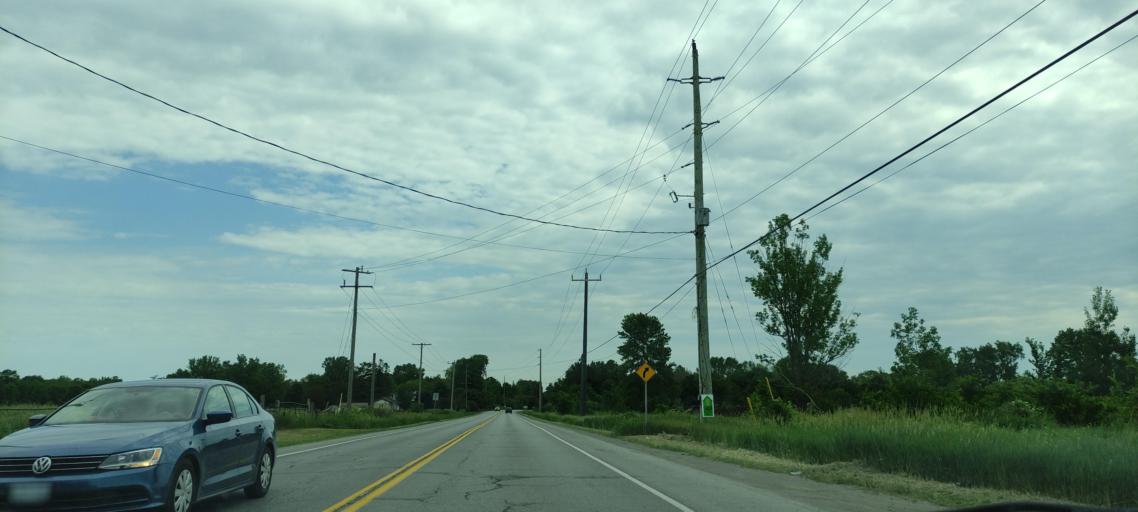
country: CA
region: Ontario
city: Quinte West
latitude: 44.0703
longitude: -77.5998
